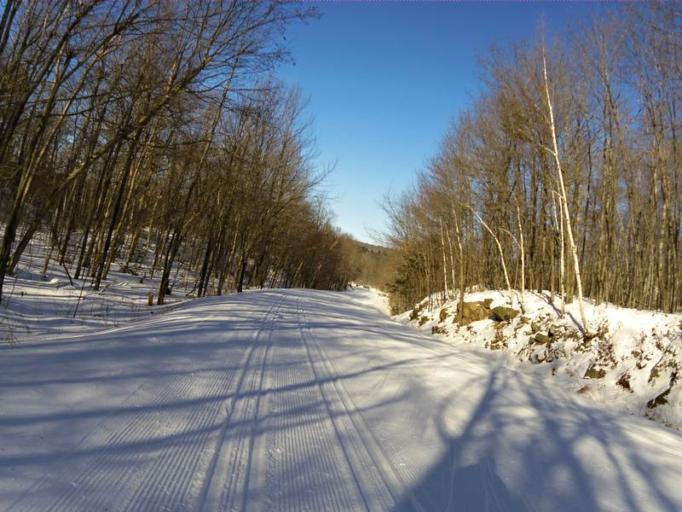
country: CA
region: Quebec
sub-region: Outaouais
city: Gatineau
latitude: 45.4753
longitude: -75.8452
